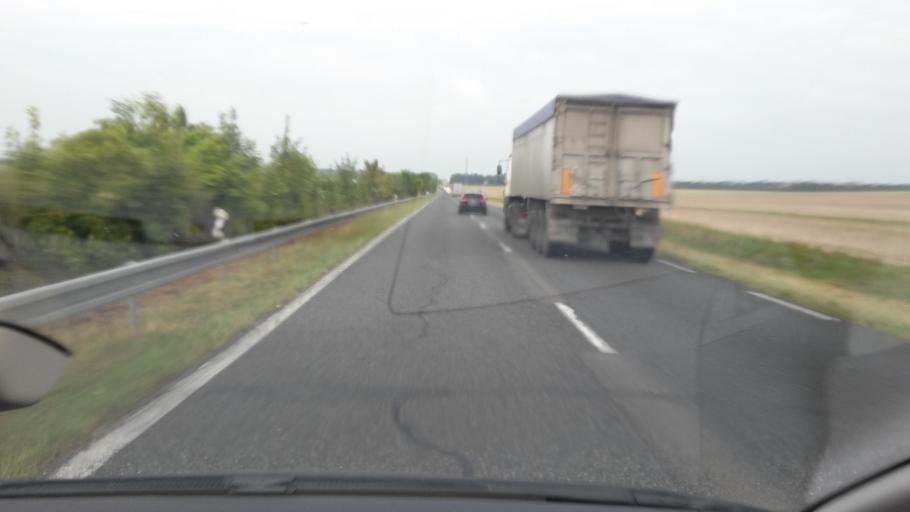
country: FR
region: Champagne-Ardenne
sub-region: Departement de la Marne
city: Warmeriville
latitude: 49.3748
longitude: 4.2197
